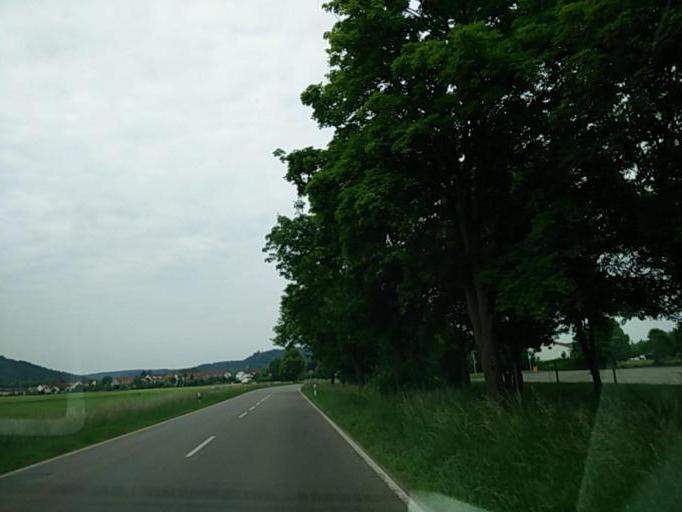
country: DE
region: Baden-Wuerttemberg
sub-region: Tuebingen Region
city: Tuebingen
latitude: 48.4865
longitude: 9.0047
